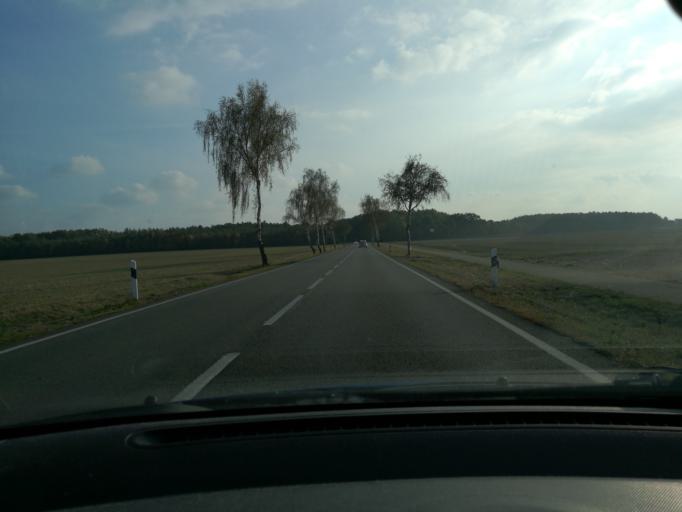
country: DE
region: Lower Saxony
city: Kusten
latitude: 53.0039
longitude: 11.1053
